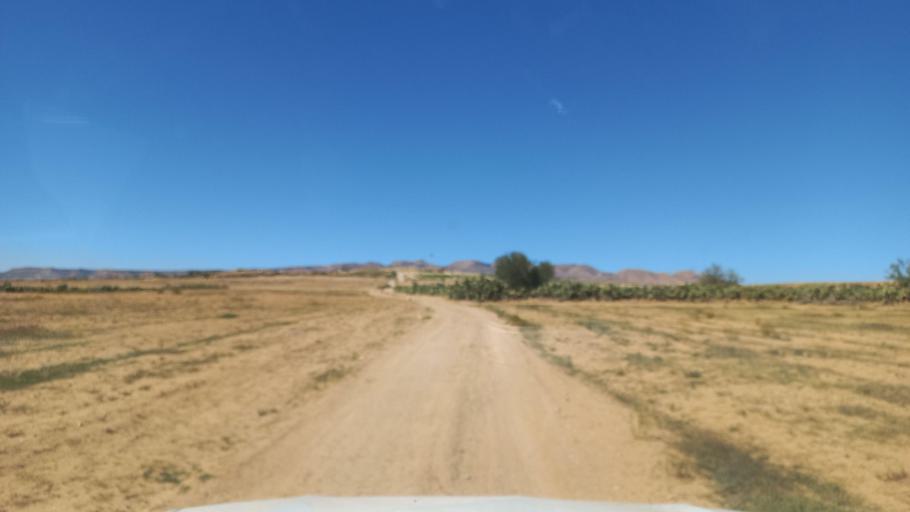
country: TN
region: Al Qasrayn
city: Sbiba
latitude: 35.3715
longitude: 9.0833
